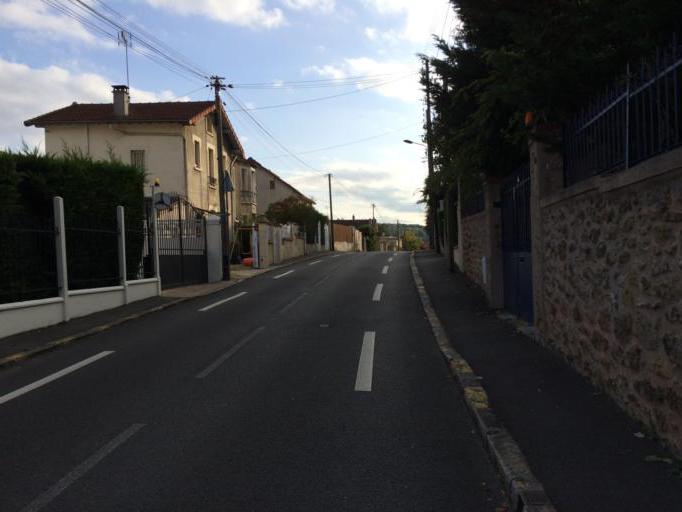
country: FR
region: Ile-de-France
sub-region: Departement de l'Essonne
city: Villebon-sur-Yvette
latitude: 48.7078
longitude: 2.2368
